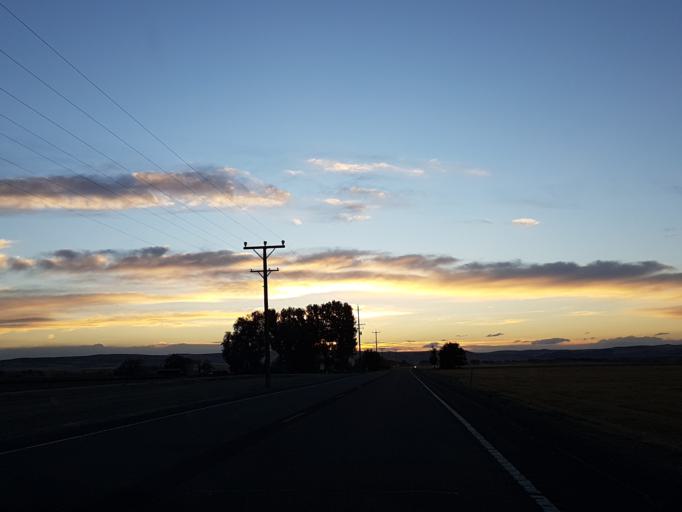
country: US
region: Oregon
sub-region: Malheur County
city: Vale
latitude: 43.9391
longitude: -117.3418
